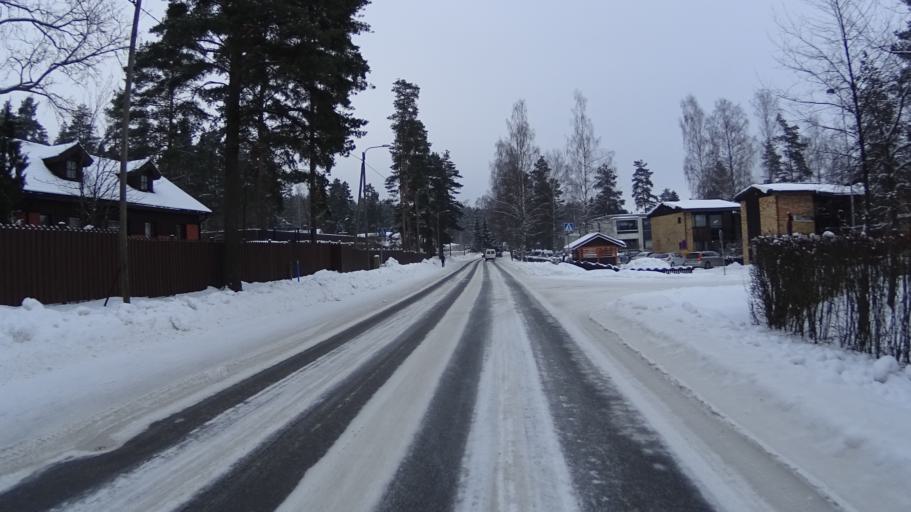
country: FI
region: Uusimaa
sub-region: Helsinki
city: Vihti
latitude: 60.3307
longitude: 24.3002
